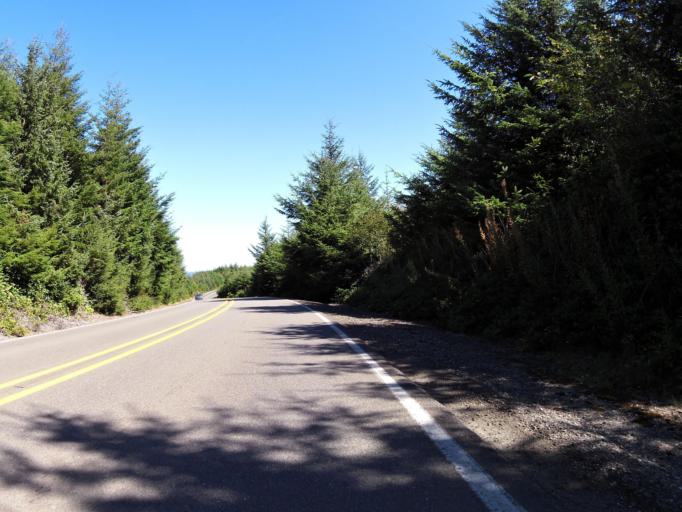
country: US
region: Oregon
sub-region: Coos County
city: Barview
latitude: 43.2703
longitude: -124.3525
